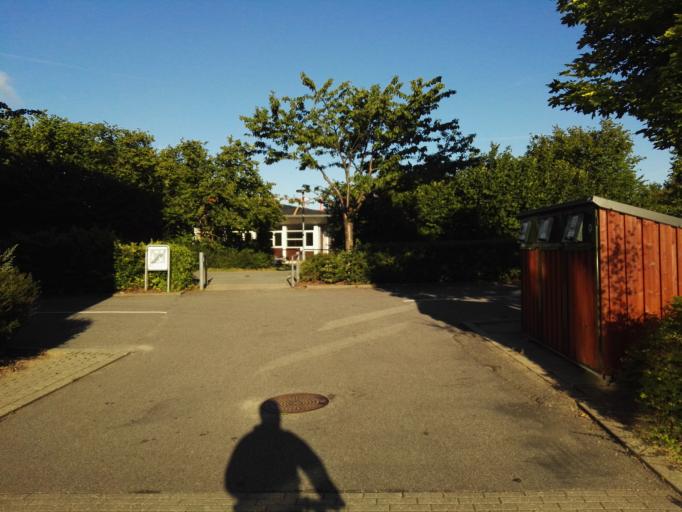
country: DK
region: Capital Region
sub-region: Ballerup Kommune
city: Ballerup
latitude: 55.7250
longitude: 12.3626
